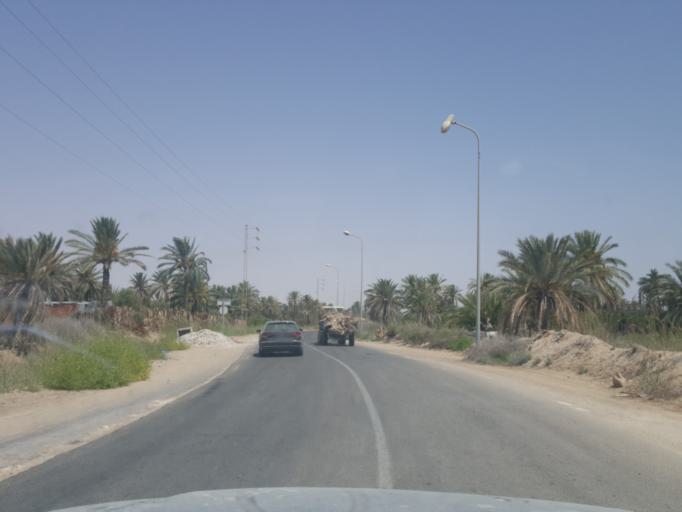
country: TN
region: Qabis
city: Gabes
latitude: 33.9654
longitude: 9.9995
